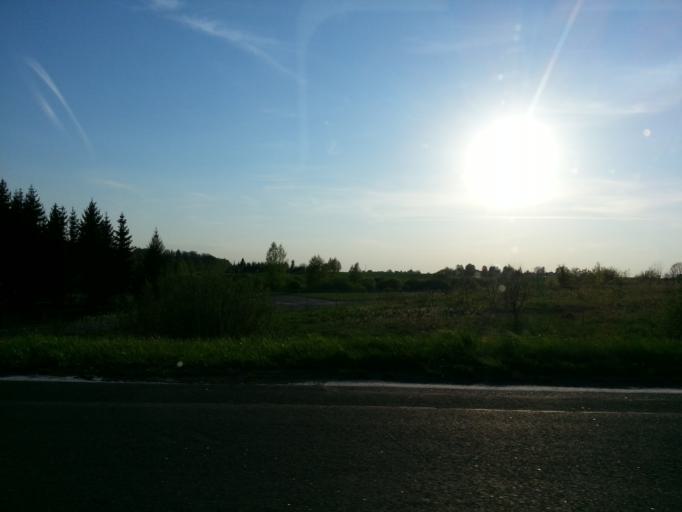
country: LT
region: Vilnius County
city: Ukmerge
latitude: 55.1818
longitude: 24.8108
